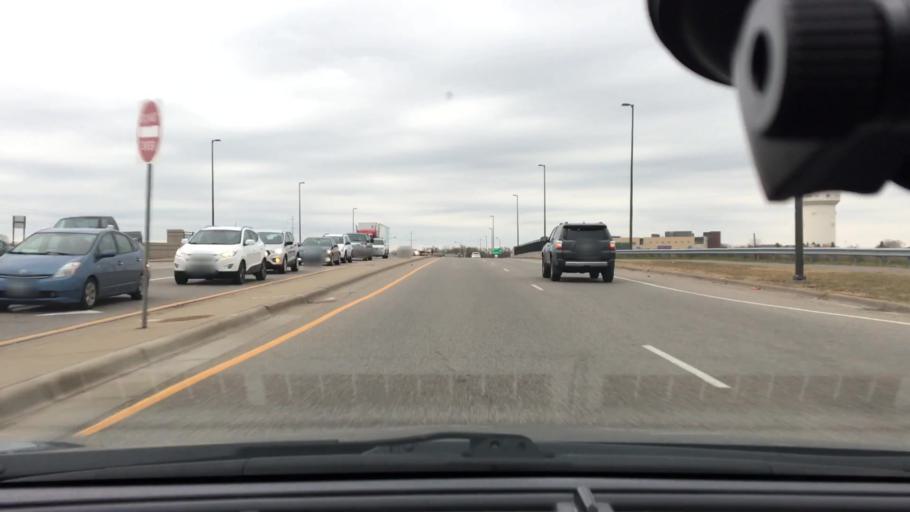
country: US
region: Minnesota
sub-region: Hennepin County
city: Maple Grove
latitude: 45.1274
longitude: -93.4874
